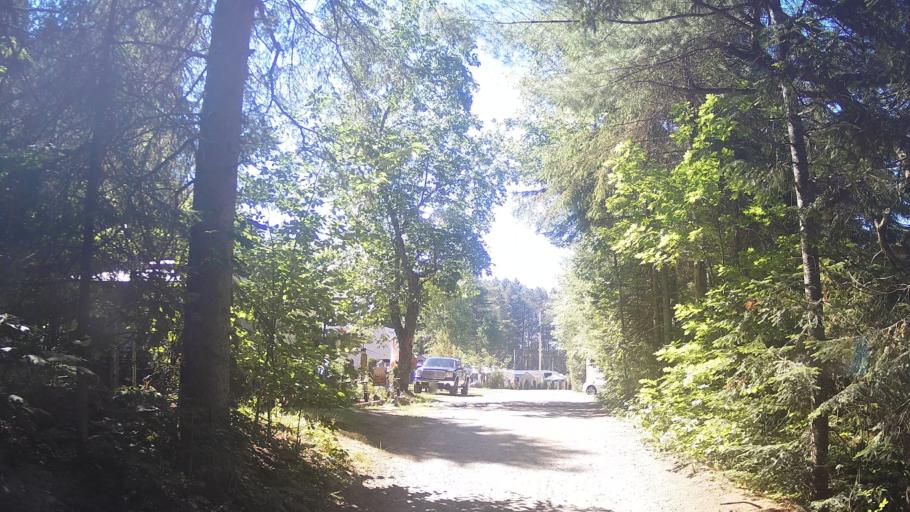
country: CA
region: Ontario
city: Huntsville
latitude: 45.3762
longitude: -79.2145
